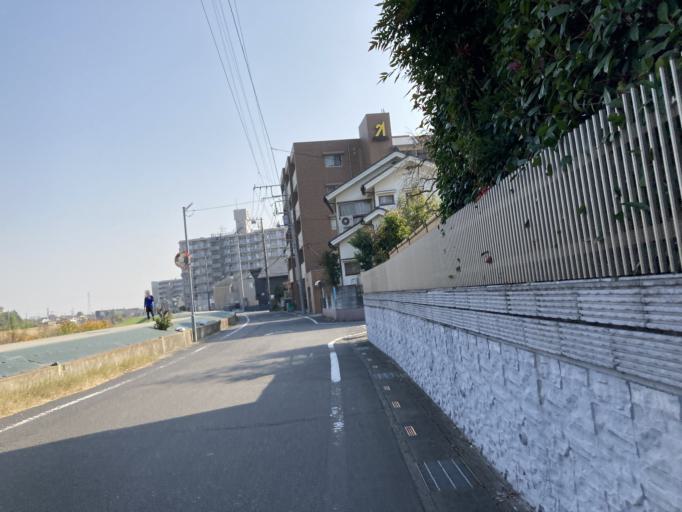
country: JP
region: Saitama
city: Koshigaya
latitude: 35.8816
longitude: 139.7478
